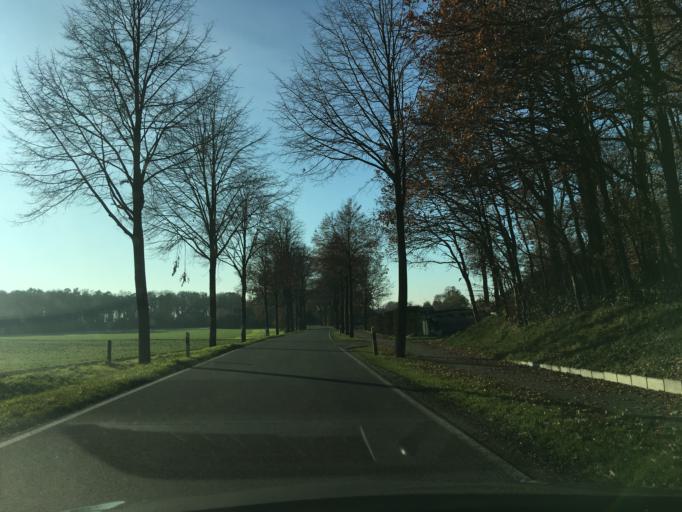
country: DE
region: North Rhine-Westphalia
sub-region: Regierungsbezirk Munster
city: Vreden
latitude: 52.1106
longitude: 6.8801
